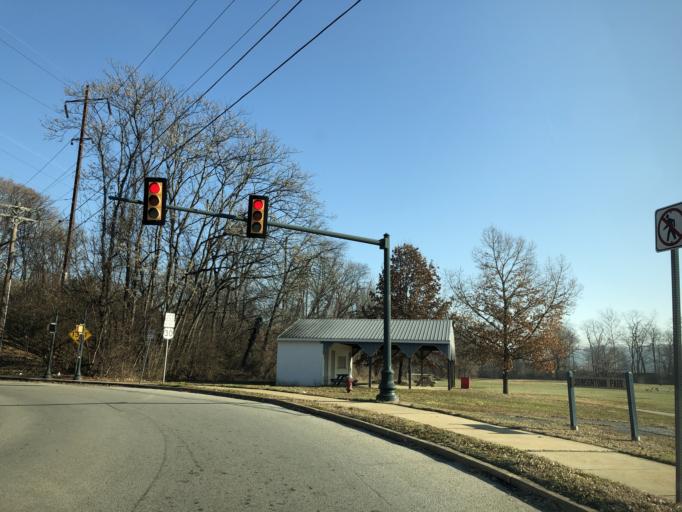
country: US
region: Pennsylvania
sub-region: Chester County
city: Downingtown
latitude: 40.0022
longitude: -75.7080
